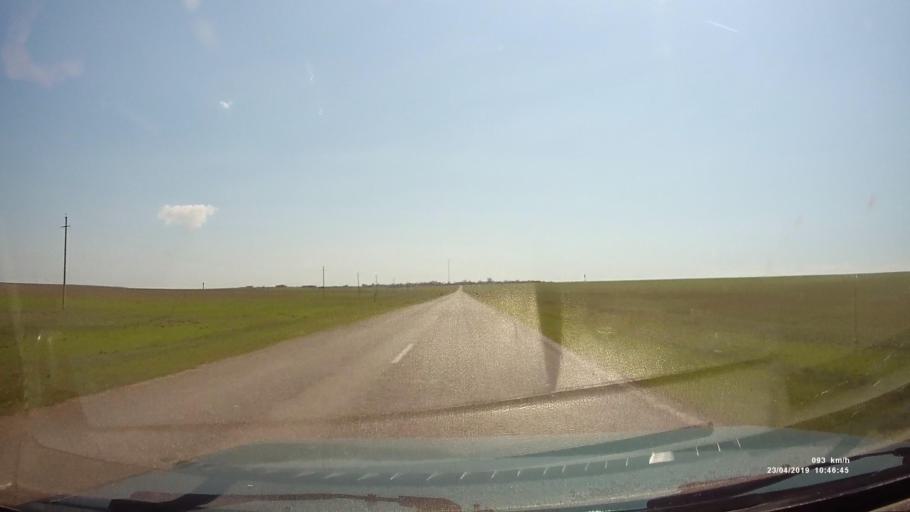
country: RU
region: Kalmykiya
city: Yashalta
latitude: 46.4405
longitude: 42.6961
